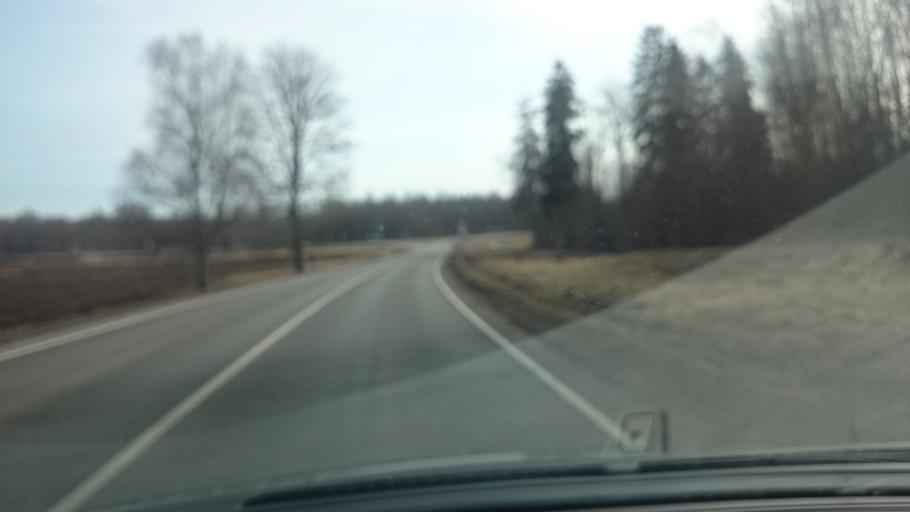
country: EE
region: Jaervamaa
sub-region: Paide linn
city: Paide
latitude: 58.8819
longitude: 25.5177
